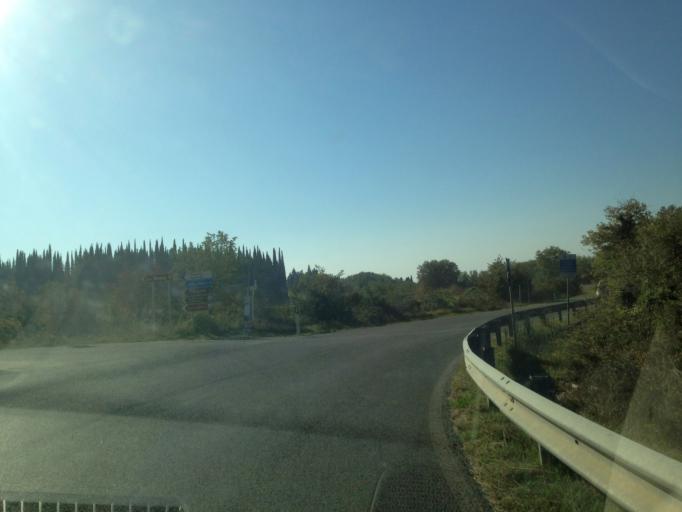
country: IT
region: Tuscany
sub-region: Provincia di Siena
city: Castellina in Chianti
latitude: 43.4429
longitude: 11.3011
